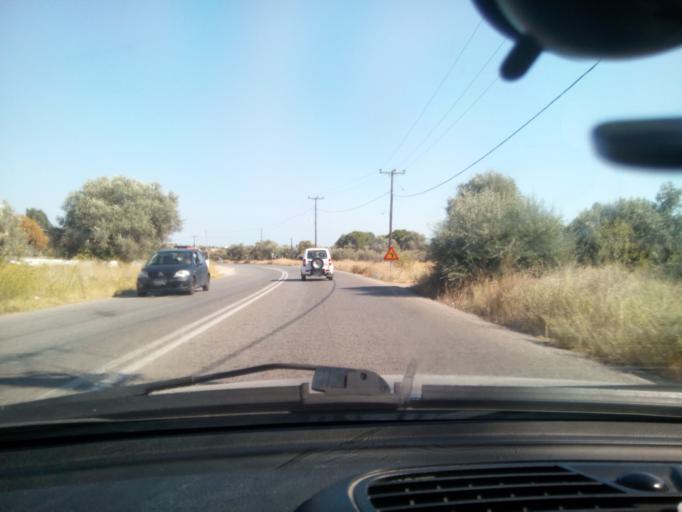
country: GR
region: Central Greece
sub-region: Nomos Evvoias
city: Malakonta
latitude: 38.4060
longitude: 23.7426
